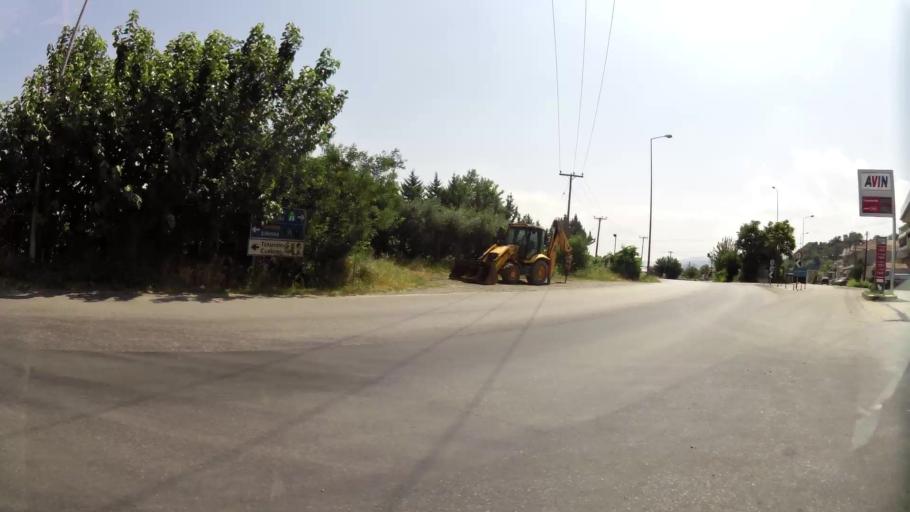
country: GR
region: Central Macedonia
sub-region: Nomos Imathias
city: Veroia
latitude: 40.5109
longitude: 22.2167
